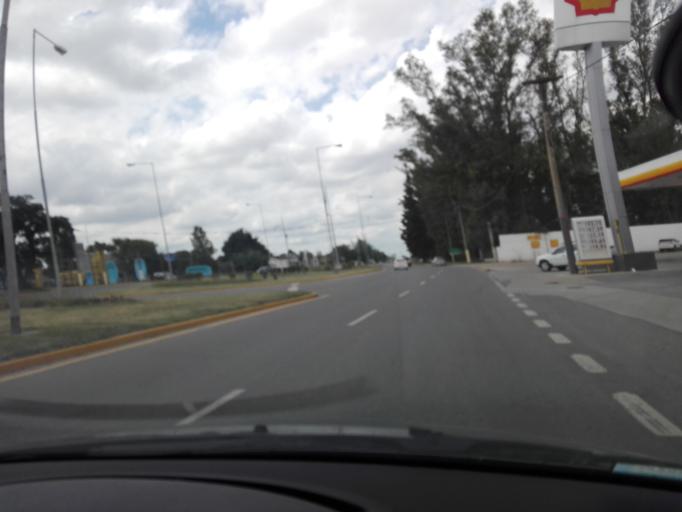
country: AR
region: Cordoba
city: Alta Gracia
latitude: -31.6514
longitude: -64.4084
